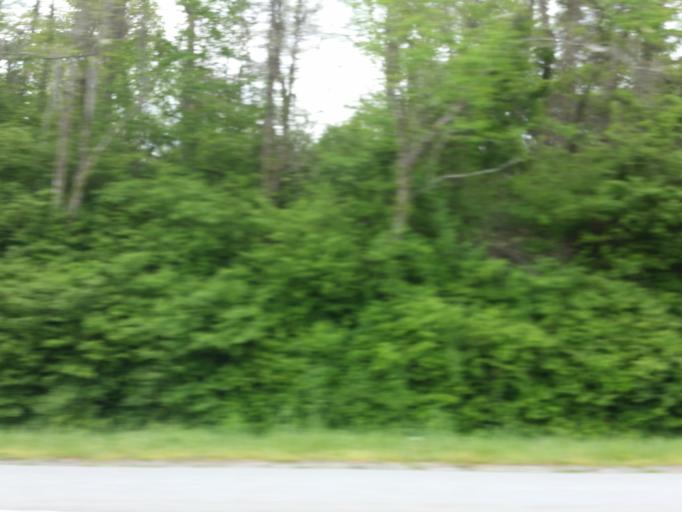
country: US
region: Kentucky
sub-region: Bell County
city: Middlesboro
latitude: 36.4877
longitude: -83.8290
